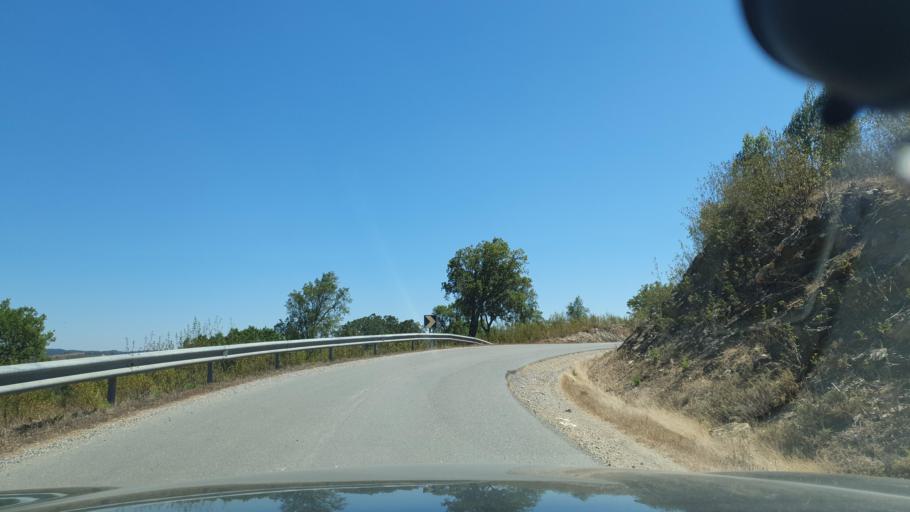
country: PT
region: Beja
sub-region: Ourique
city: Ourique
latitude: 37.5537
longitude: -8.4109
